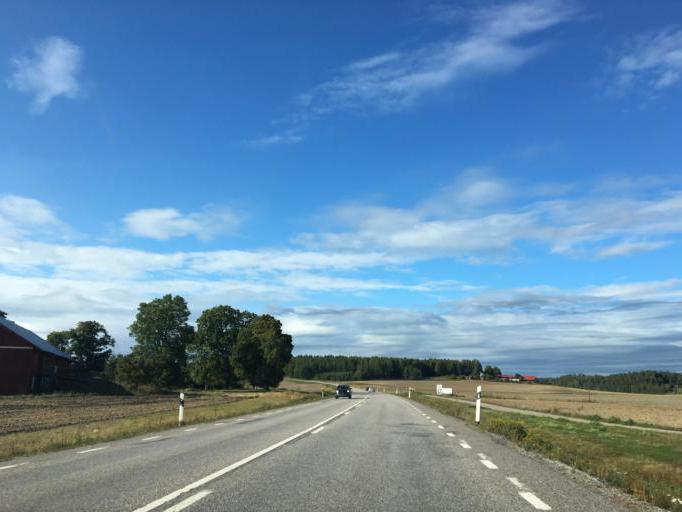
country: SE
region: Soedermanland
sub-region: Nykopings Kommun
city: Svalsta
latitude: 58.8583
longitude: 16.9166
